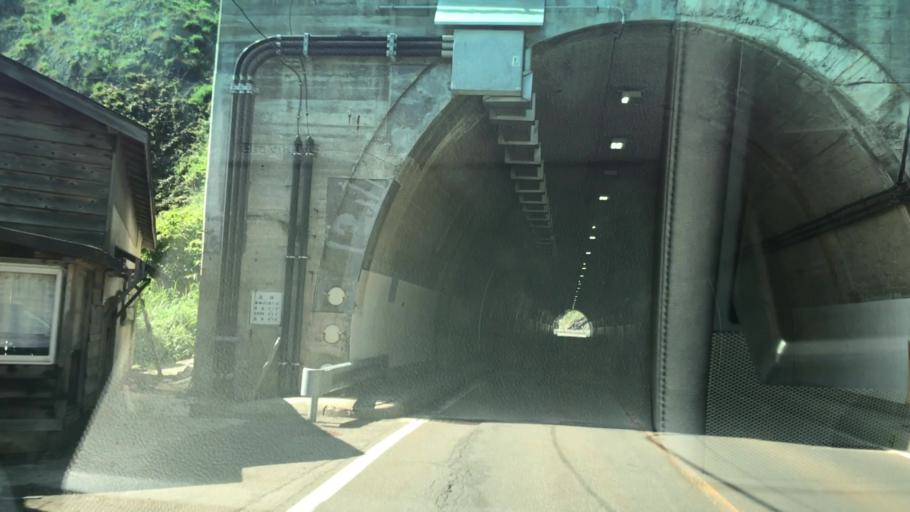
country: JP
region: Hokkaido
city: Iwanai
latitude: 43.1083
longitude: 140.4522
